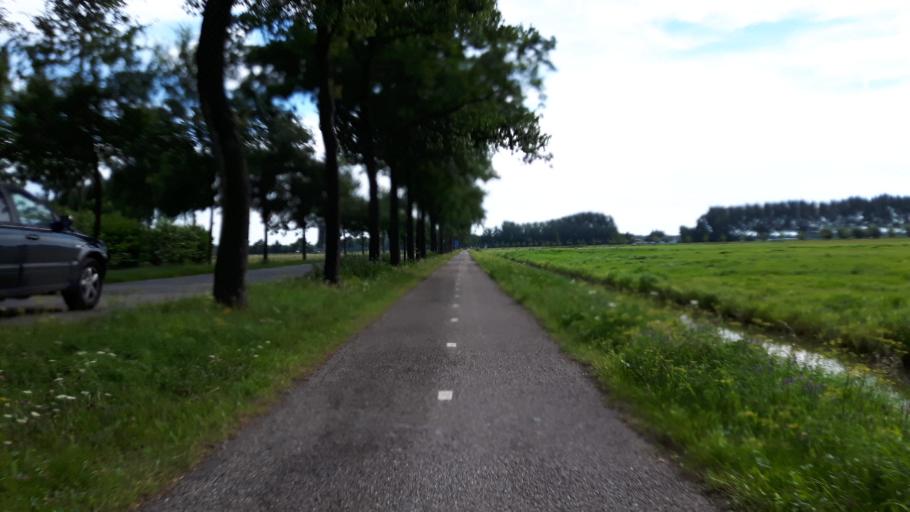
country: NL
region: Utrecht
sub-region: Stichtse Vecht
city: Spechtenkamp
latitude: 52.1188
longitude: 4.9824
